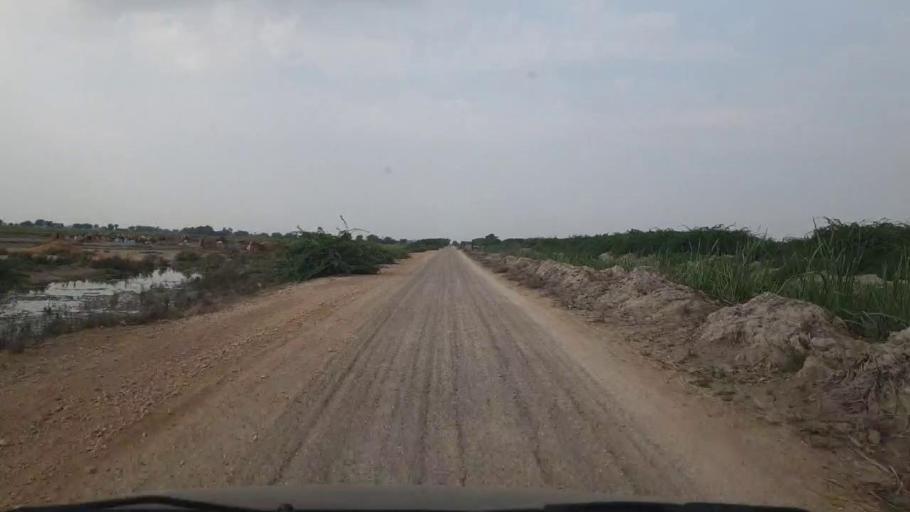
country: PK
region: Sindh
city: Kario
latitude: 24.6017
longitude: 68.6016
